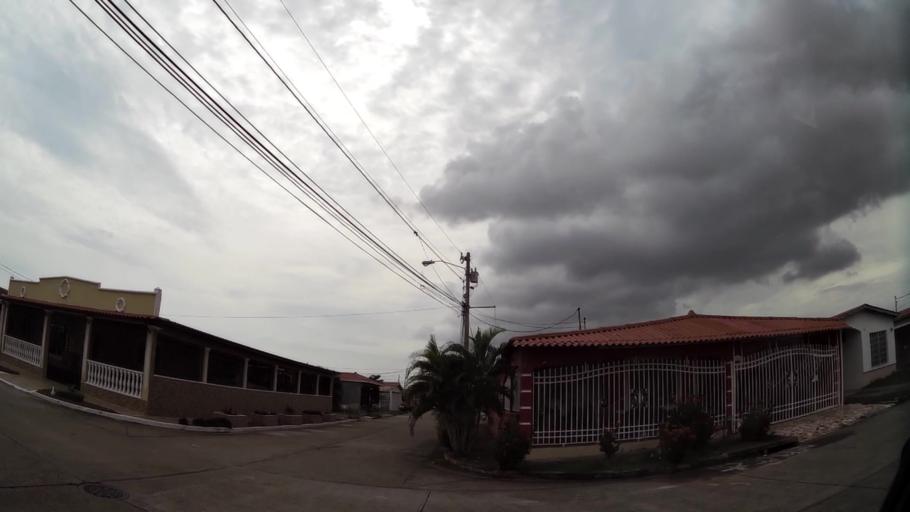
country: PA
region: Panama
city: Tocumen
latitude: 9.0453
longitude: -79.4073
